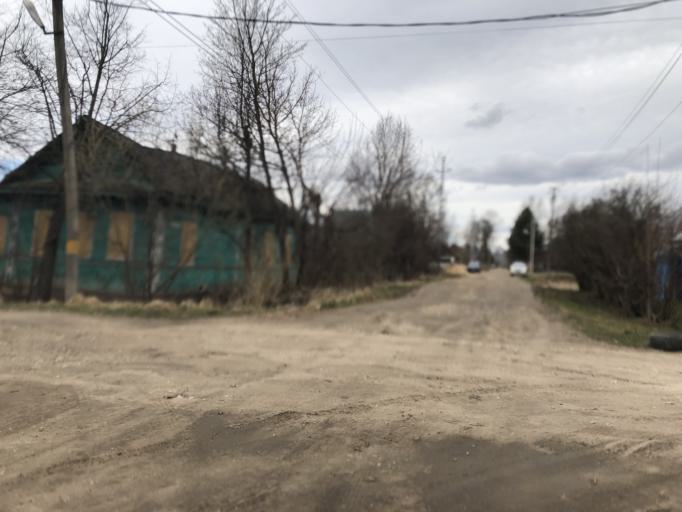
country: RU
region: Tverskaya
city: Rzhev
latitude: 56.2499
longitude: 34.3170
